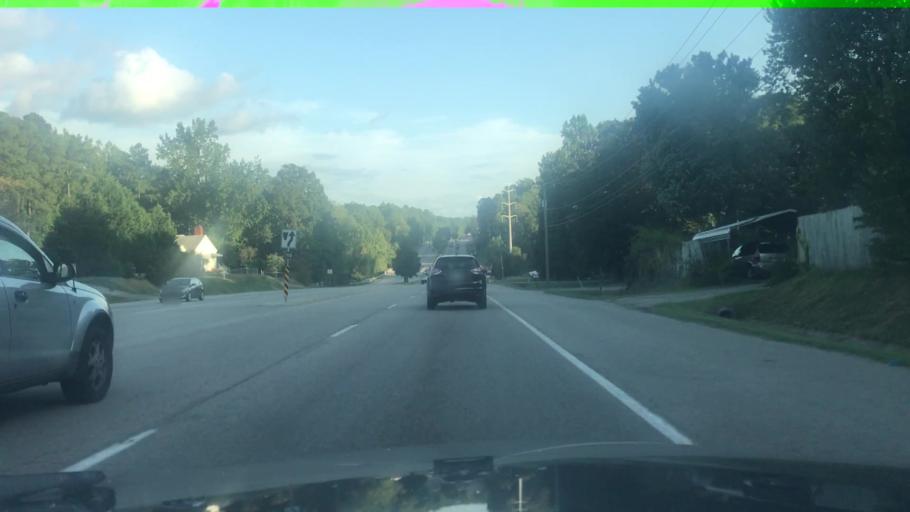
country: US
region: Virginia
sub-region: Chesterfield County
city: Brandermill
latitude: 37.4569
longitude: -77.5899
